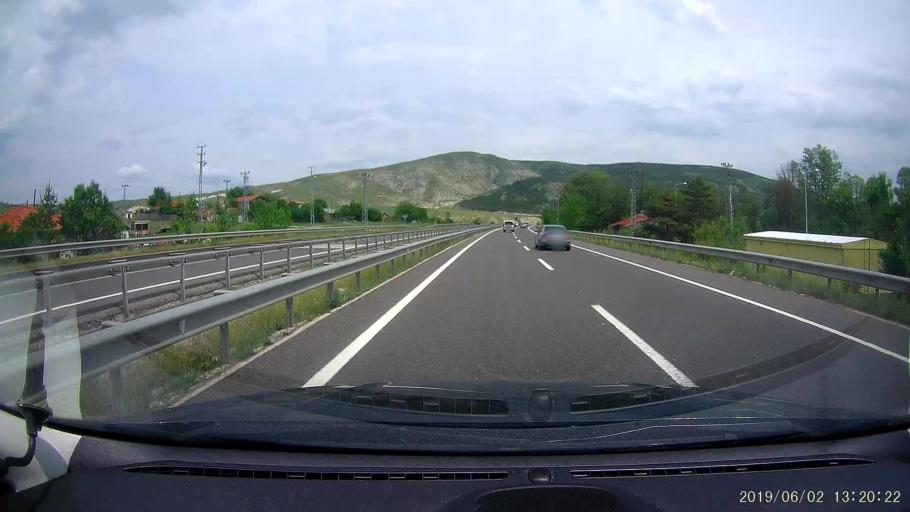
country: TR
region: Cankiri
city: Cerkes
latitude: 40.8412
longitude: 32.7579
